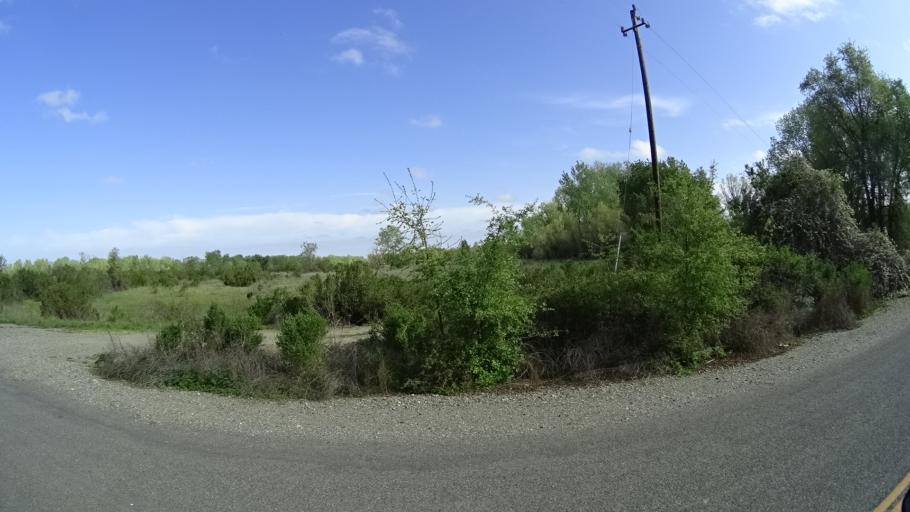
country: US
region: California
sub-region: Butte County
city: Durham
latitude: 39.5225
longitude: -121.9633
